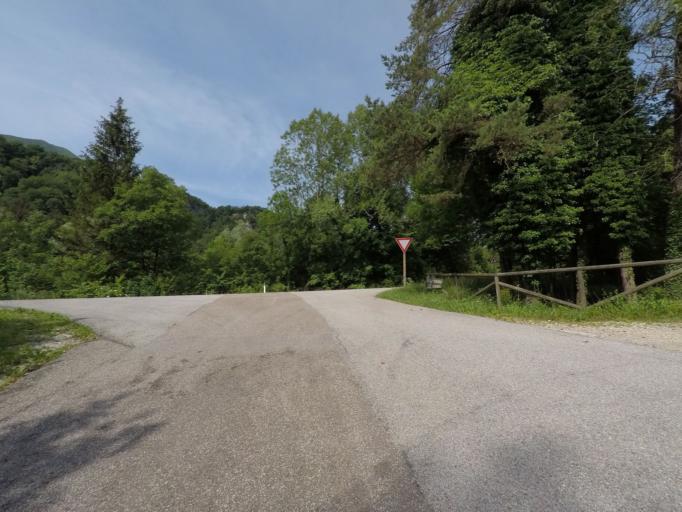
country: IT
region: Friuli Venezia Giulia
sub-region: Provincia di Udine
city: Cavazzo Carnico
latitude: 46.3589
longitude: 13.0530
